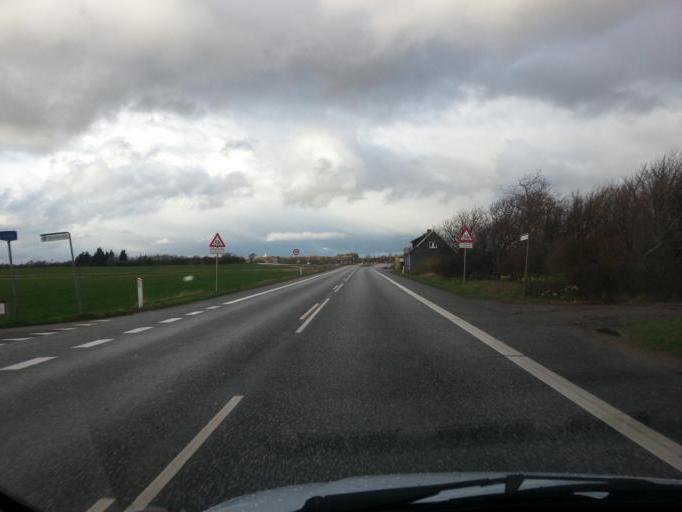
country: DK
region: Central Jutland
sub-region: Holstebro Kommune
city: Ulfborg
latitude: 56.2885
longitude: 8.3360
